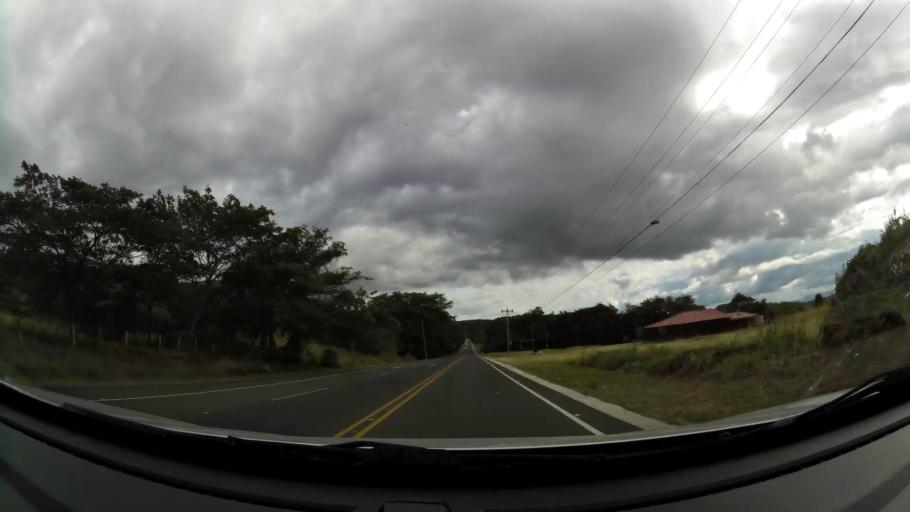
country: CR
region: Guanacaste
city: Nandayure
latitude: 10.2502
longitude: -85.2285
